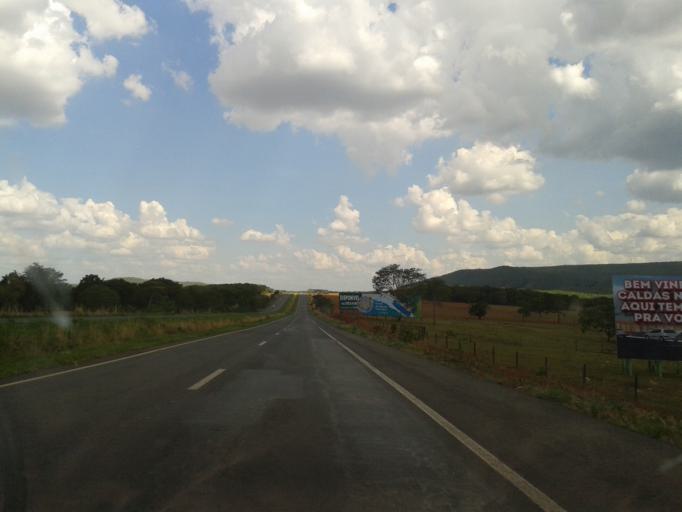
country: BR
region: Goias
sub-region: Caldas Novas
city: Caldas Novas
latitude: -17.7057
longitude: -48.7032
